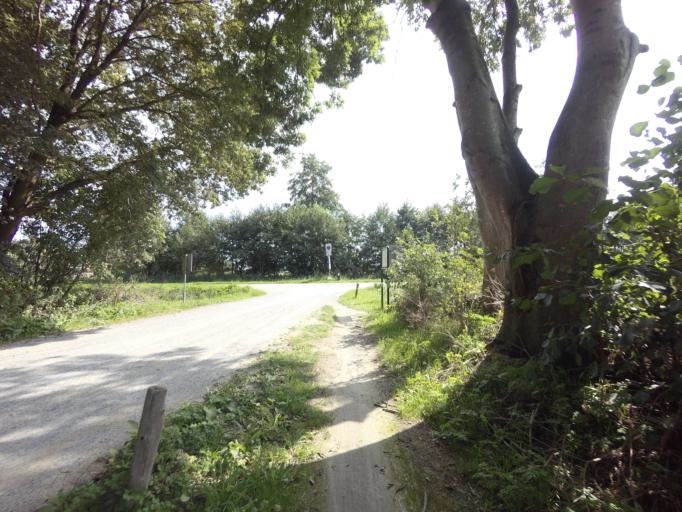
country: NL
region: Drenthe
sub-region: Gemeente Westerveld
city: Dwingeloo
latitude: 52.8799
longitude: 6.4153
